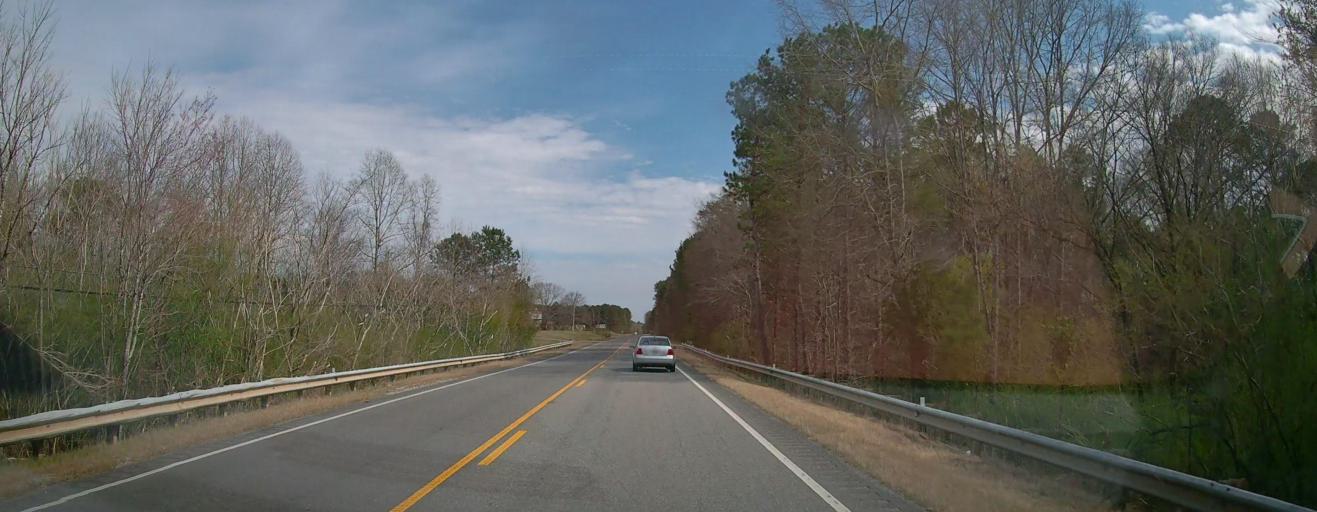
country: US
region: Alabama
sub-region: Walker County
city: Carbon Hill
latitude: 33.9090
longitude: -87.5569
